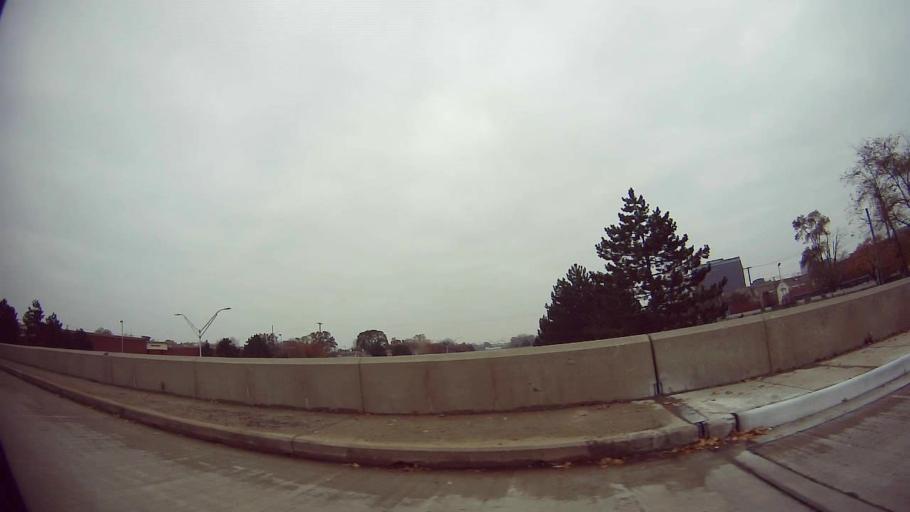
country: US
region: Michigan
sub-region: Oakland County
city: Bingham Farms
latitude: 42.4854
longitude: -83.2612
